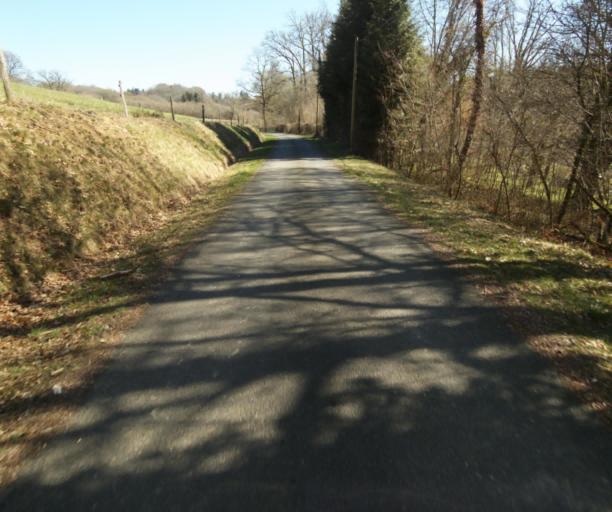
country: FR
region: Limousin
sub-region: Departement de la Correze
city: Chamboulive
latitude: 45.4068
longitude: 1.6362
